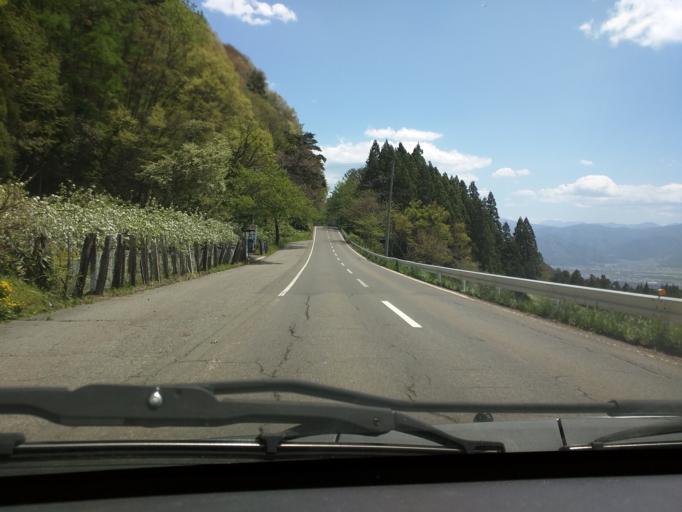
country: JP
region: Nagano
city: Nagano-shi
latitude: 36.6835
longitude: 138.1627
